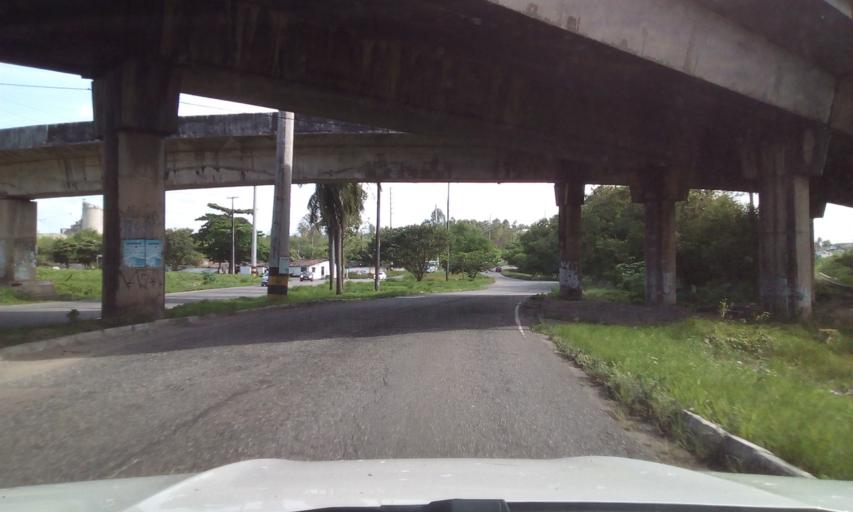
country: BR
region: Paraiba
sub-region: Joao Pessoa
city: Joao Pessoa
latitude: -7.1230
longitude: -34.8934
